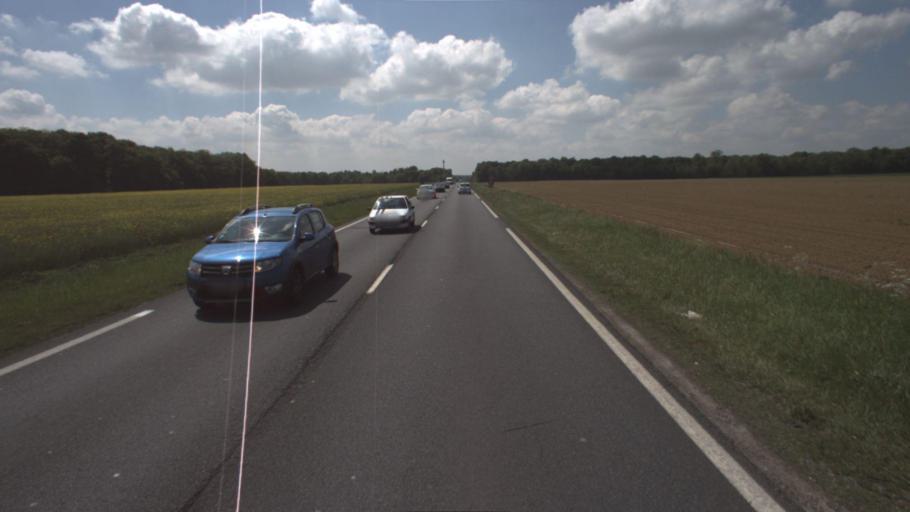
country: FR
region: Ile-de-France
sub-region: Departement de Seine-et-Marne
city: Chaumes-en-Brie
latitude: 48.6748
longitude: 2.8131
